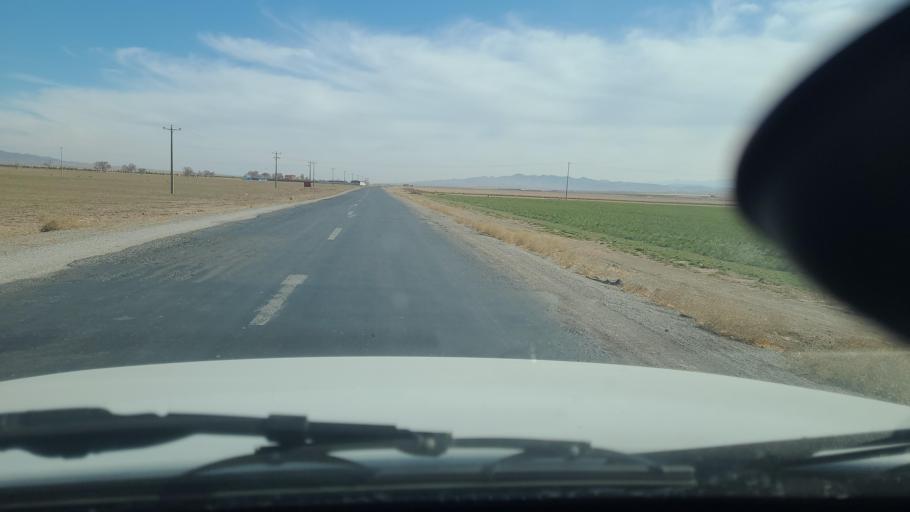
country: IR
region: Razavi Khorasan
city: Dowlatabad
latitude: 35.6002
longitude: 59.4619
